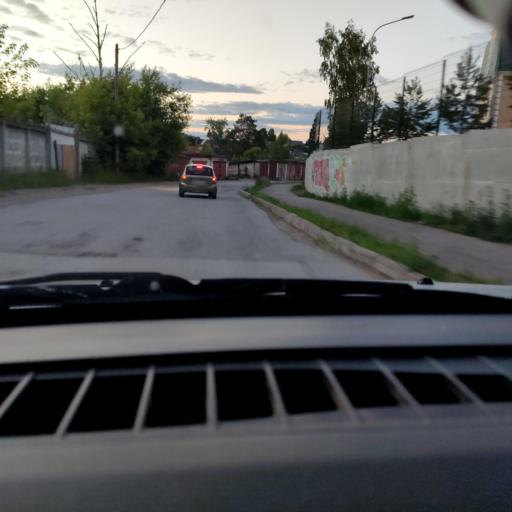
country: RU
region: Perm
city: Perm
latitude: 58.1150
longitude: 56.3093
